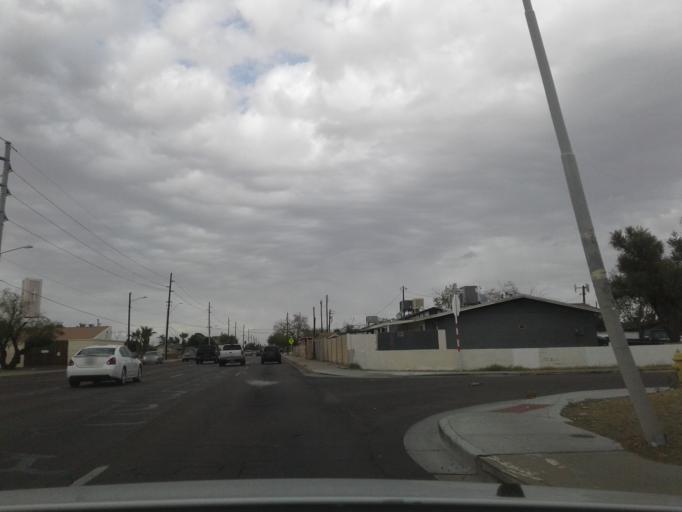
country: US
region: Arizona
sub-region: Maricopa County
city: Glendale
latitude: 33.4756
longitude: -112.1859
